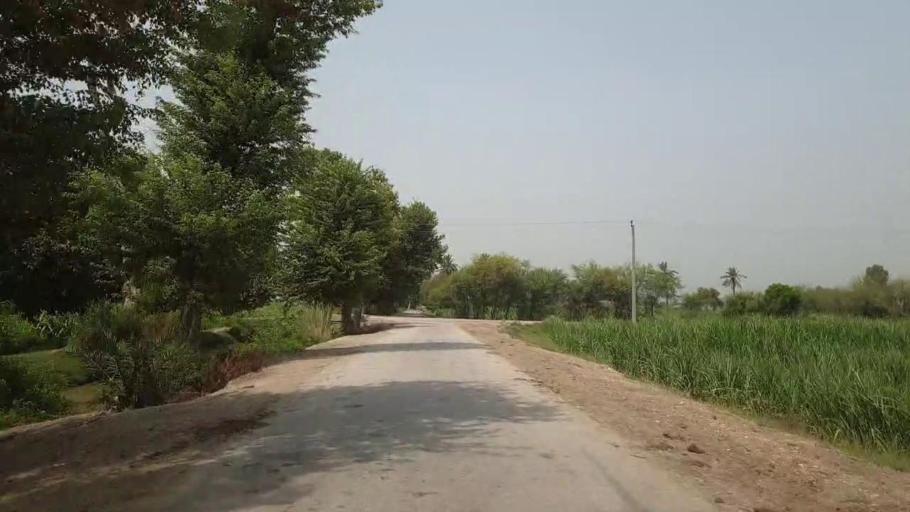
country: PK
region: Sindh
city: Gambat
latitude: 27.4384
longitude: 68.4884
